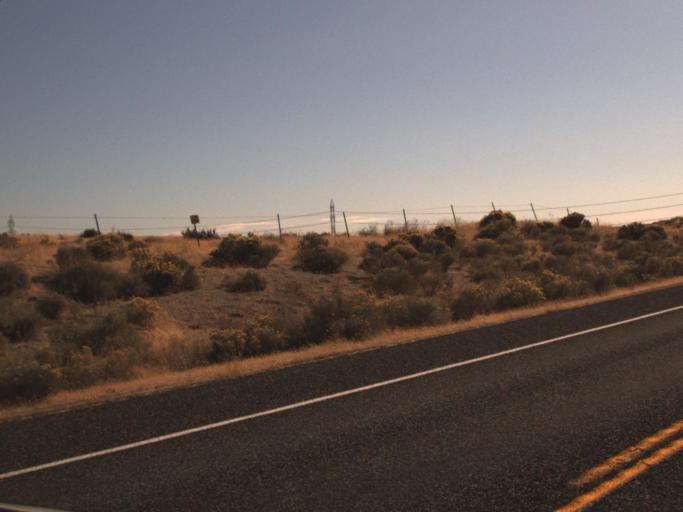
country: US
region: Washington
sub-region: Benton County
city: West Richland
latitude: 46.4021
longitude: -119.4455
